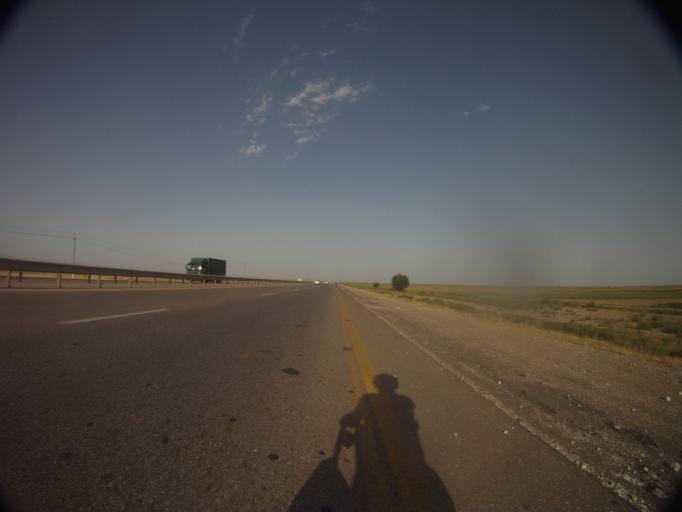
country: AZ
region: Goranboy
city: Goranboy
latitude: 40.6441
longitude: 46.7102
